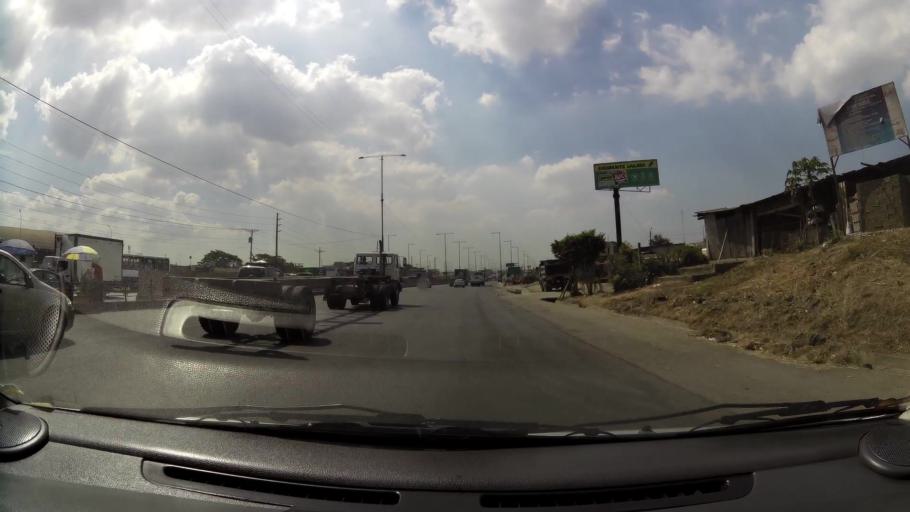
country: EC
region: Guayas
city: Santa Lucia
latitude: -2.1254
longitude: -79.9495
